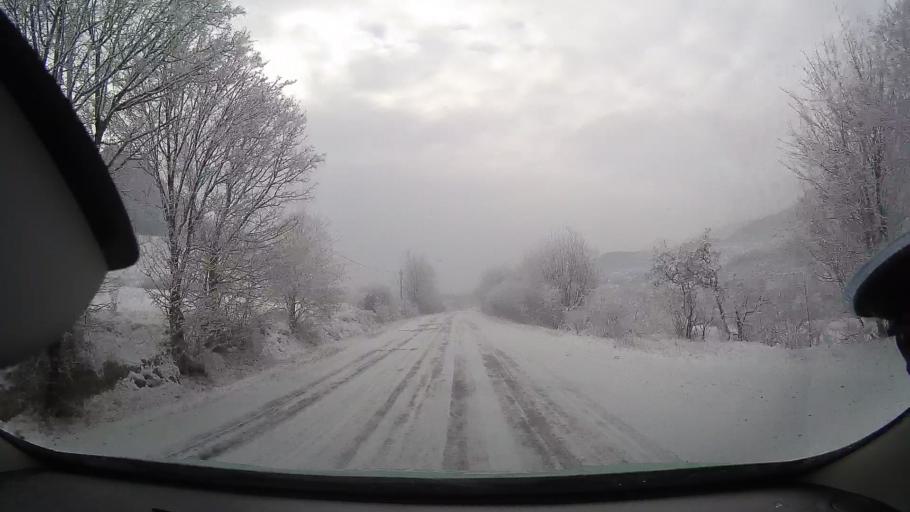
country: RO
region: Alba
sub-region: Comuna Rimetea
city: Rimetea
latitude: 46.4619
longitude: 23.5722
